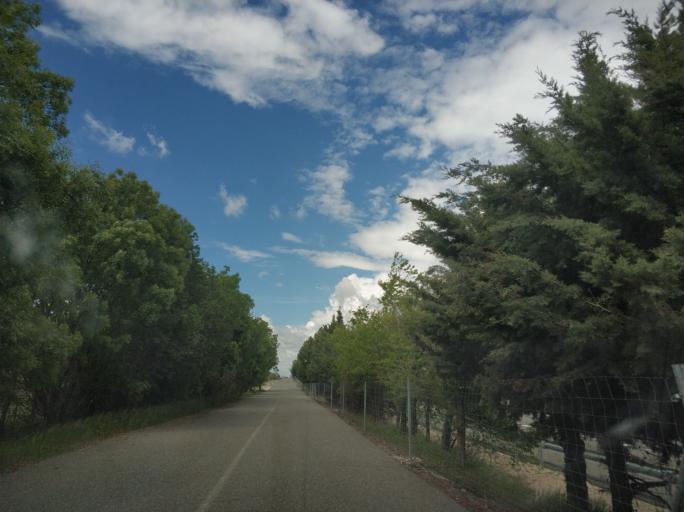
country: ES
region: Castille and Leon
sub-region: Provincia de Salamanca
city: Sorihuela
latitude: 40.4567
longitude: -5.6804
